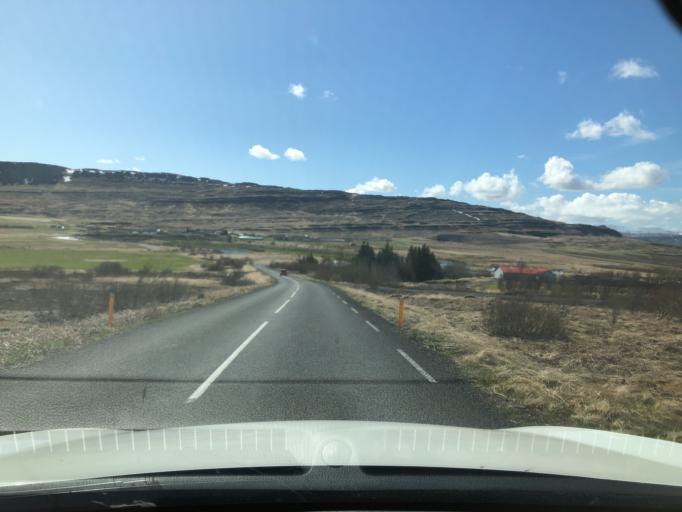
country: IS
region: West
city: Borgarnes
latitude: 64.6668
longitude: -21.4079
